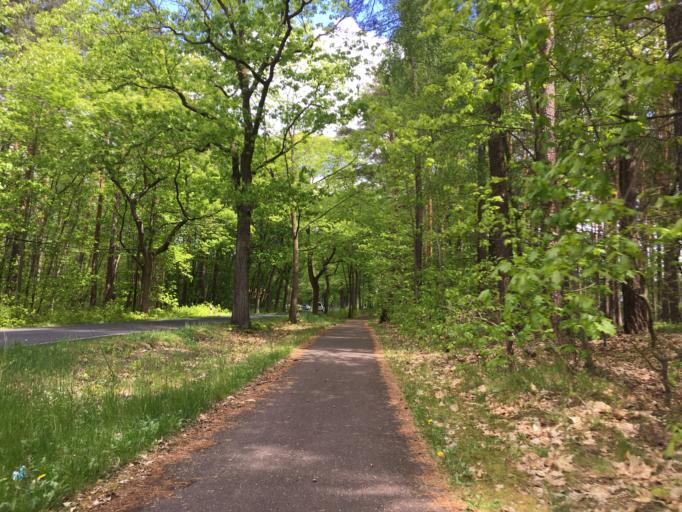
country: DE
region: Brandenburg
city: Marienwerder
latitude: 52.8964
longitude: 13.5049
